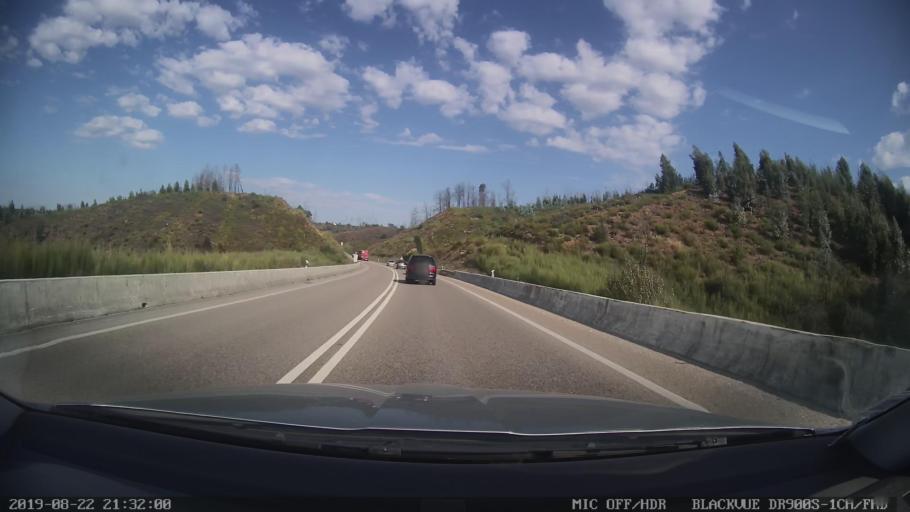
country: PT
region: Leiria
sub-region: Pedrogao Grande
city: Pedrogao Grande
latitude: 39.9252
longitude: -8.1587
